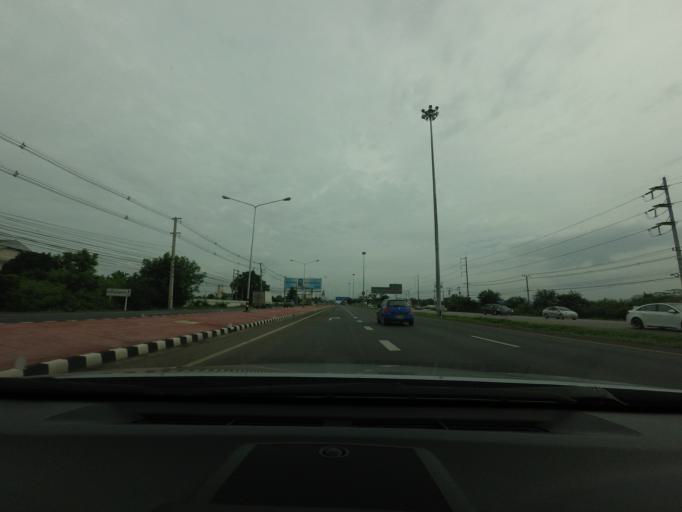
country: TH
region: Ratchaburi
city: Pak Tho
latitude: 13.3317
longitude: 99.8298
